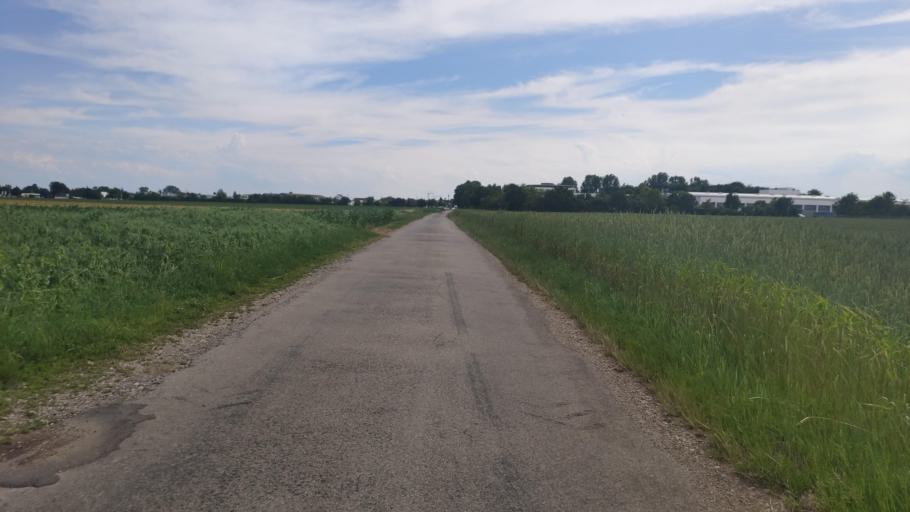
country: DE
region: Bavaria
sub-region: Swabia
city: Konigsbrunn
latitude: 48.2614
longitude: 10.8759
